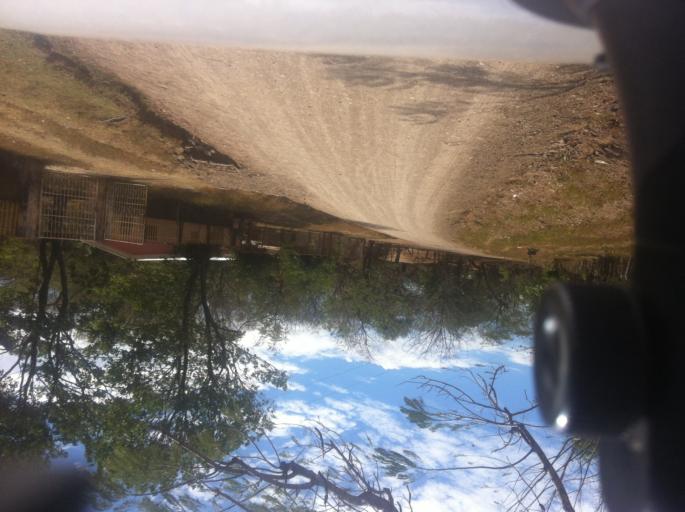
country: NI
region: Granada
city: Nandaime
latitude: 11.6077
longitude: -86.0350
